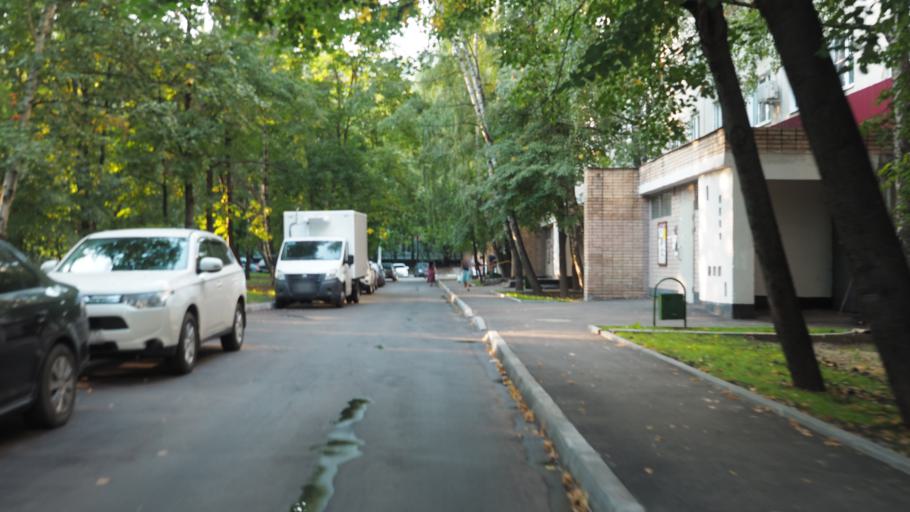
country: RU
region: Moscow
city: Orekhovo-Borisovo
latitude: 55.6014
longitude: 37.7143
